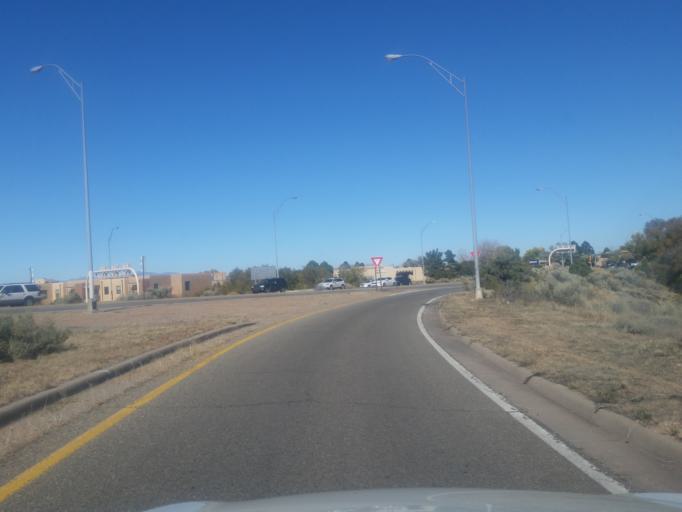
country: US
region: New Mexico
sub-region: Santa Fe County
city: Santa Fe
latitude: 35.6598
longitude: -105.9561
